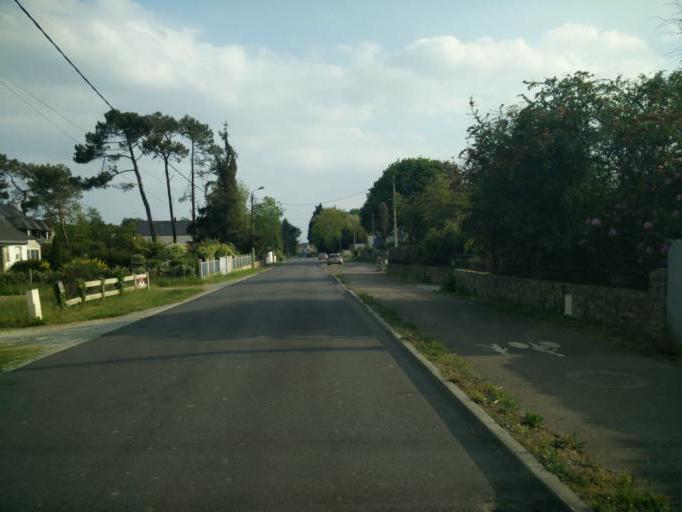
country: FR
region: Brittany
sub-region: Departement du Morbihan
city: Ploemeur
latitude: 47.7175
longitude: -3.4362
